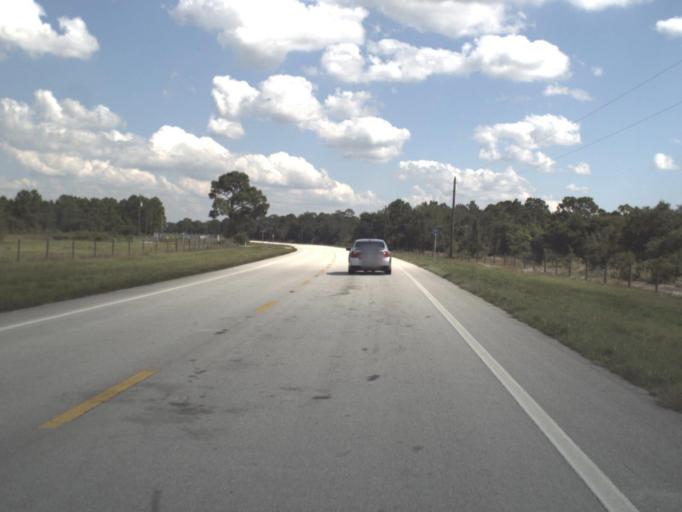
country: US
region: Florida
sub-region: Highlands County
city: Lake Placid
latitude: 27.3823
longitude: -81.1280
